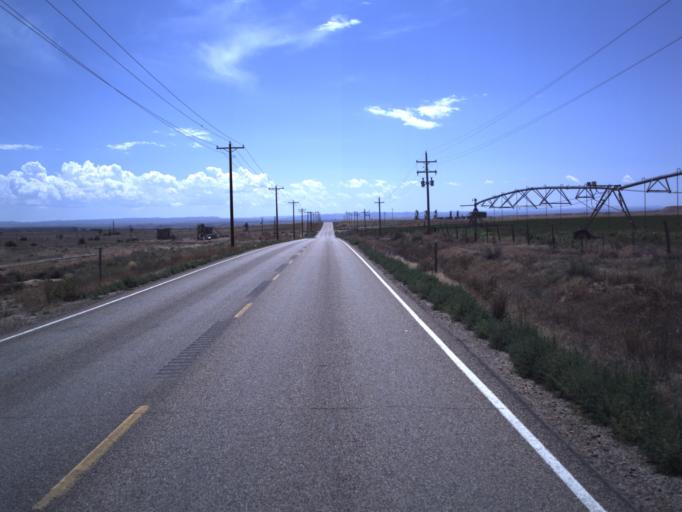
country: US
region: Utah
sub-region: Uintah County
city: Naples
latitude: 40.1639
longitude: -109.6644
